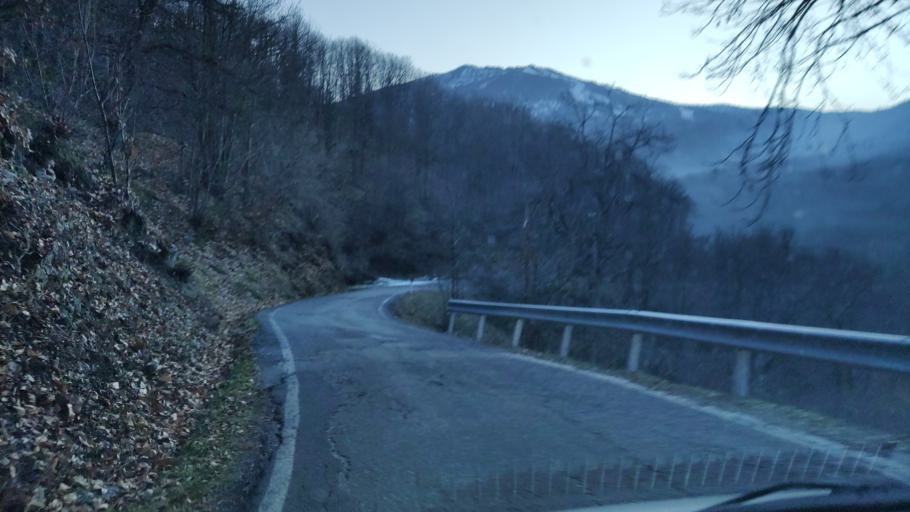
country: IT
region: Piedmont
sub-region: Provincia di Cuneo
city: Viola
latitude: 44.2908
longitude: 7.9804
